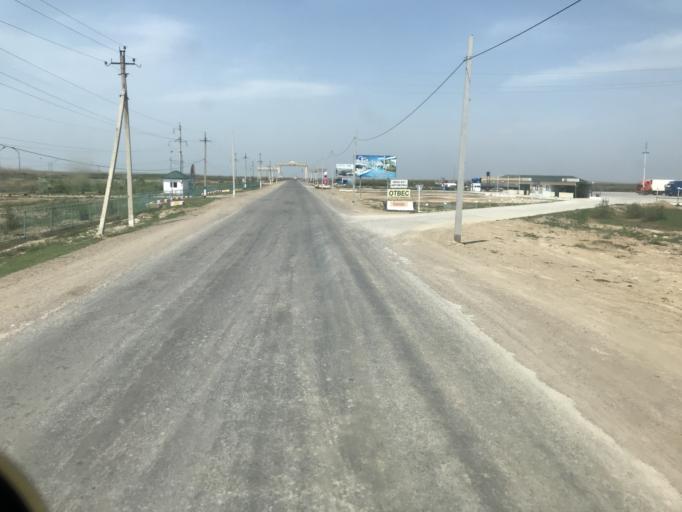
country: KZ
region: Ongtustik Qazaqstan
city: Asykata
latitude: 40.9613
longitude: 68.4609
